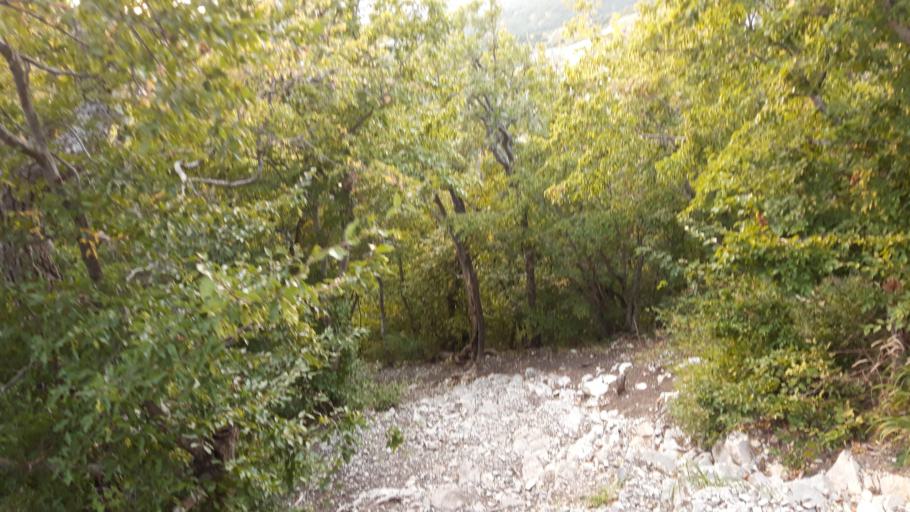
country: RU
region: Krasnodarskiy
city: Gelendzhik
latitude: 44.5834
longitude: 38.0902
